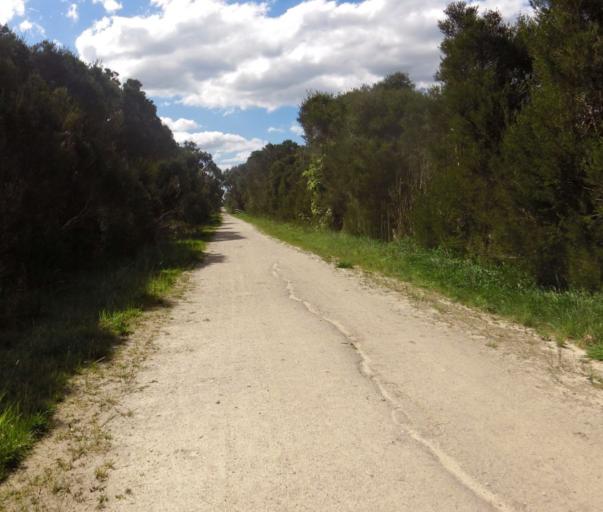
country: AU
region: Victoria
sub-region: Bass Coast
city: North Wonthaggi
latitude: -38.6480
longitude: 146.0302
